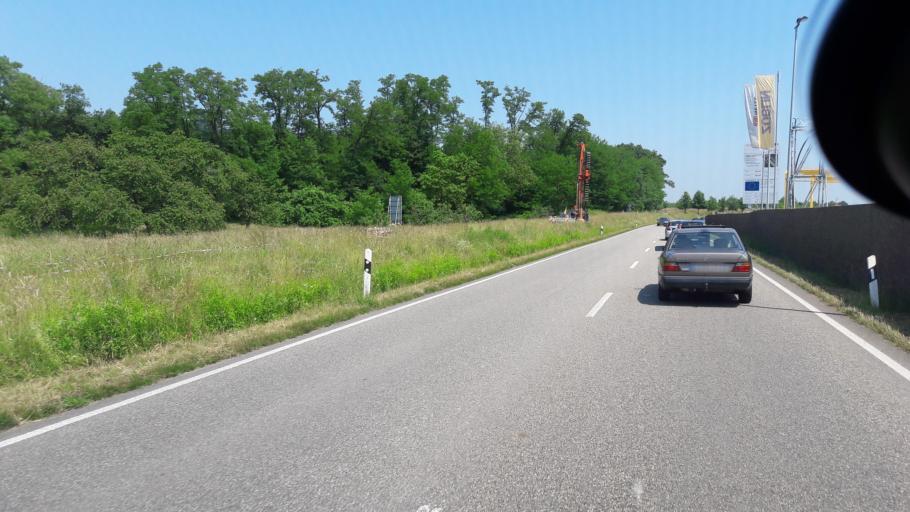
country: DE
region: Baden-Wuerttemberg
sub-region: Karlsruhe Region
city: Otigheim
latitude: 48.8736
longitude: 8.2377
